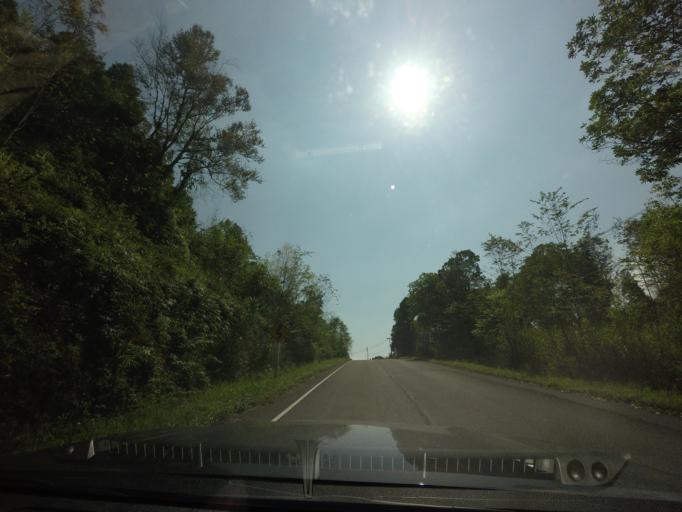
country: TH
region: Nan
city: Bo Kluea
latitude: 19.0461
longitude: 101.0904
